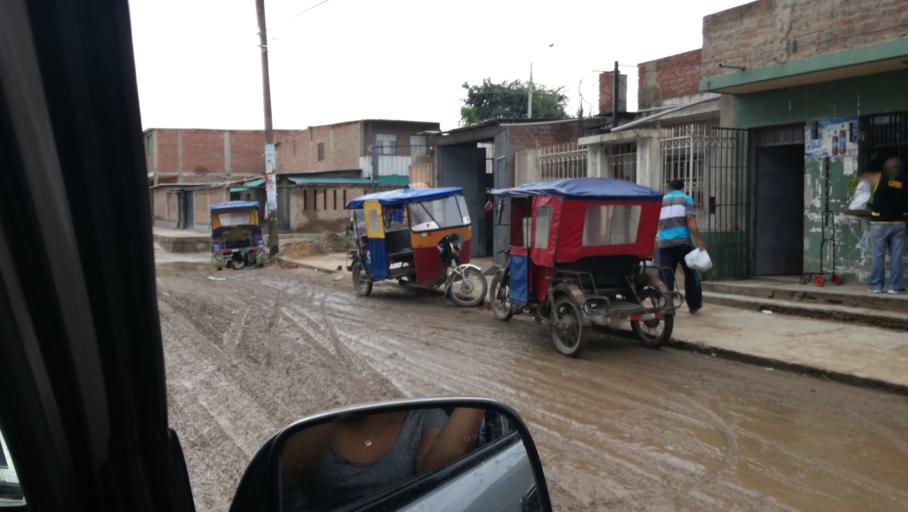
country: PE
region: Piura
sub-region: Provincia de Piura
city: Piura
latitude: -5.1895
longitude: -80.6651
